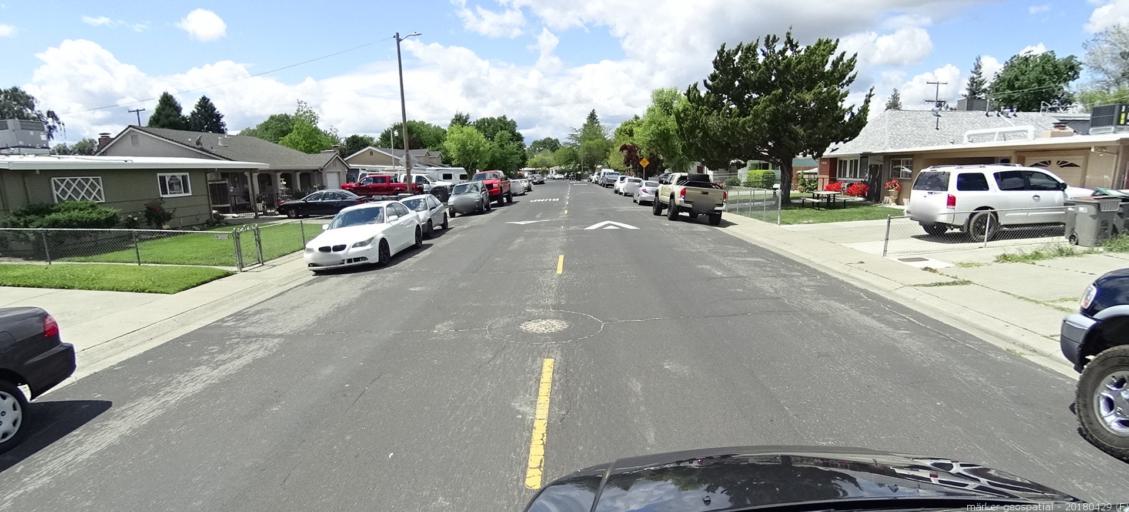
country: US
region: California
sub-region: Yolo County
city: West Sacramento
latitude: 38.5942
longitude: -121.5289
